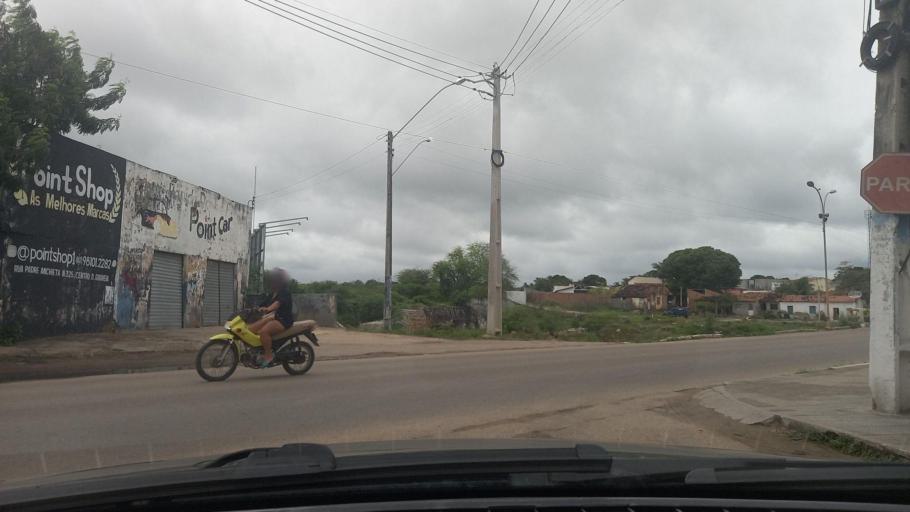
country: BR
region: Alagoas
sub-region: Delmiro Gouveia
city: Delmiro Gouveia
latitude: -9.3865
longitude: -37.9921
